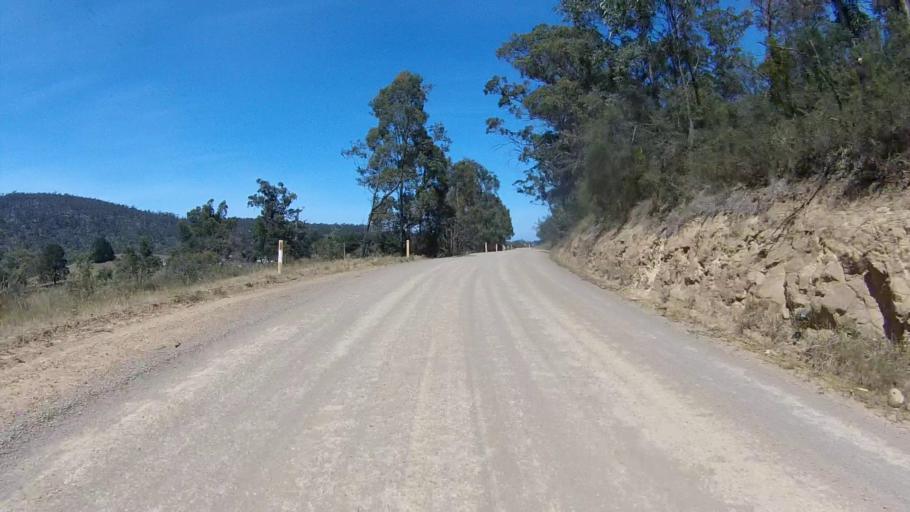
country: AU
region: Tasmania
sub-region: Sorell
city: Sorell
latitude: -42.7563
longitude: 147.6828
